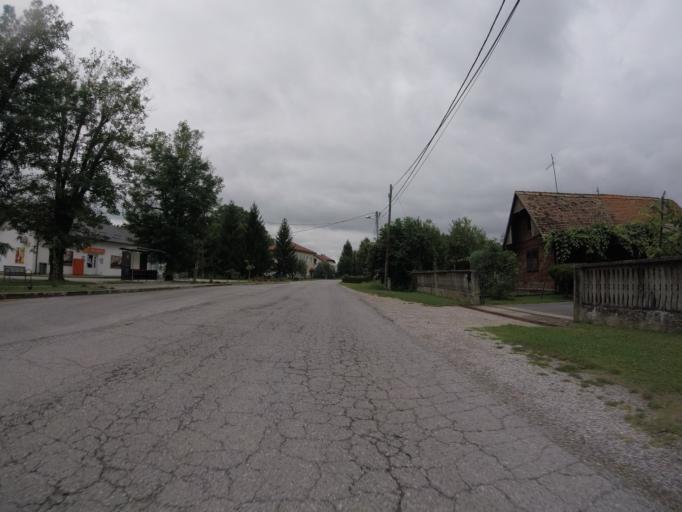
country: HR
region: Zagrebacka
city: Turopolje
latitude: 45.6528
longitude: 16.1415
